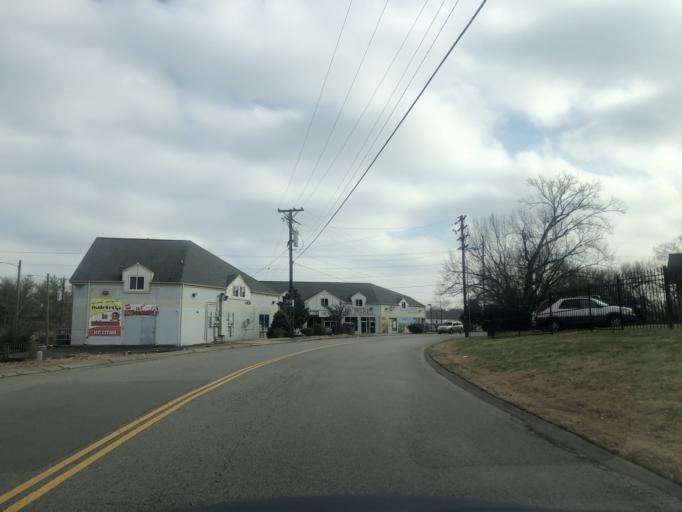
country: US
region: Tennessee
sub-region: Davidson County
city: Oak Hill
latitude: 36.0833
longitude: -86.7033
